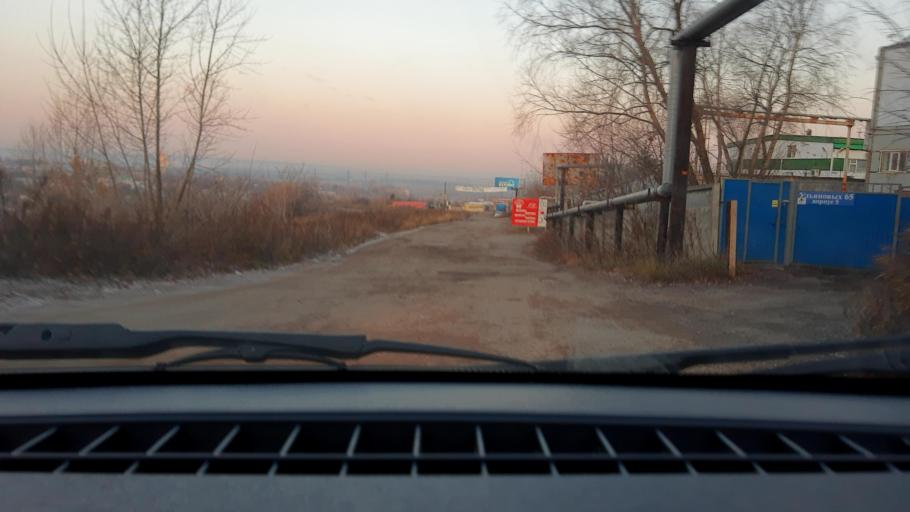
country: RU
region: Bashkortostan
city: Ufa
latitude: 54.8294
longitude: 56.0844
